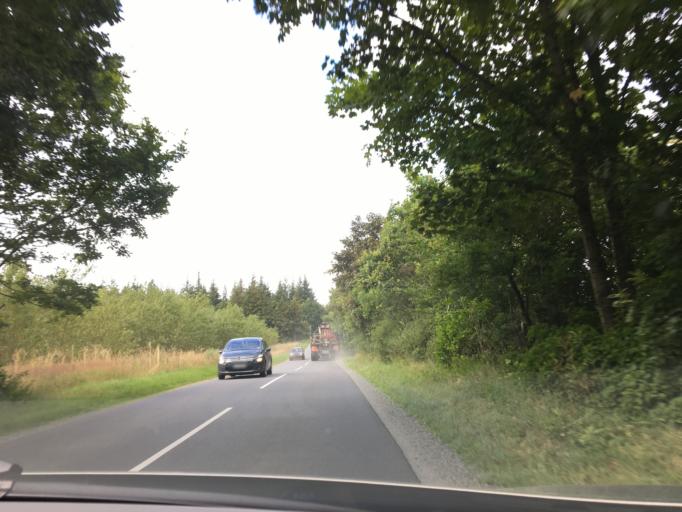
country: DK
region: South Denmark
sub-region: Varde Kommune
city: Oksbol
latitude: 55.7394
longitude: 8.2517
